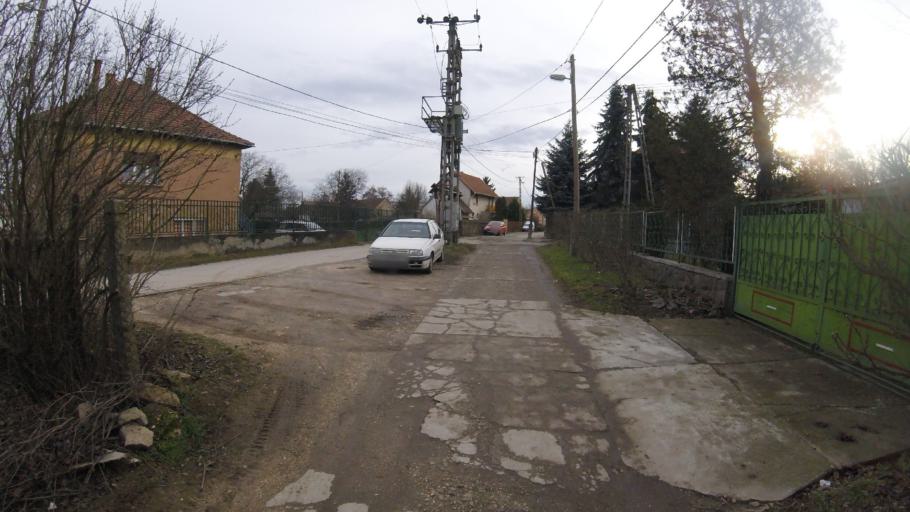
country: HU
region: Pest
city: Pomaz
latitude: 47.6499
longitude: 19.0252
